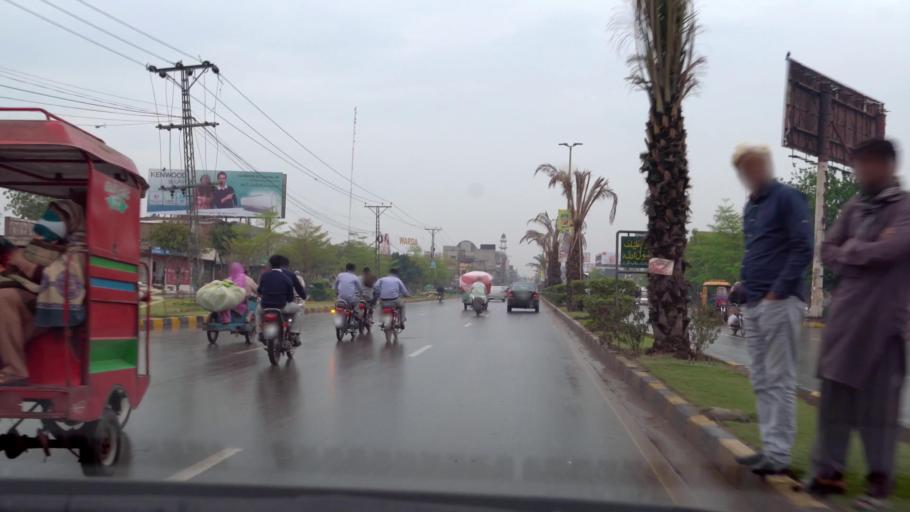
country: PK
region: Punjab
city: Faisalabad
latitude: 31.4037
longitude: 73.1038
